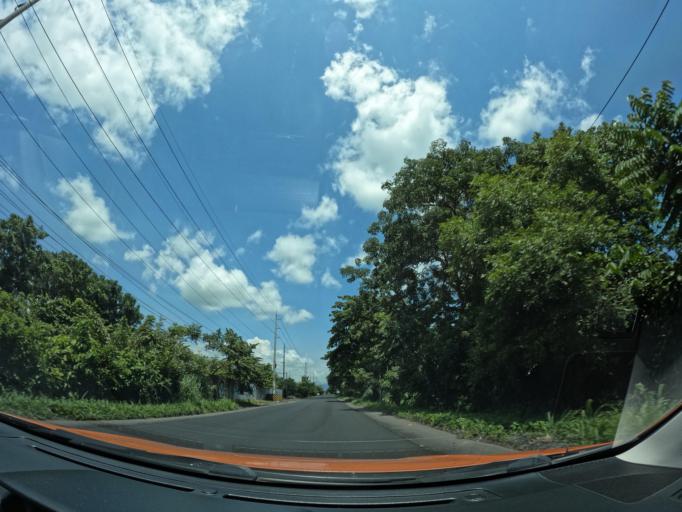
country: GT
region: Escuintla
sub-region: Municipio de Masagua
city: Masagua
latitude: 14.2289
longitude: -90.8255
